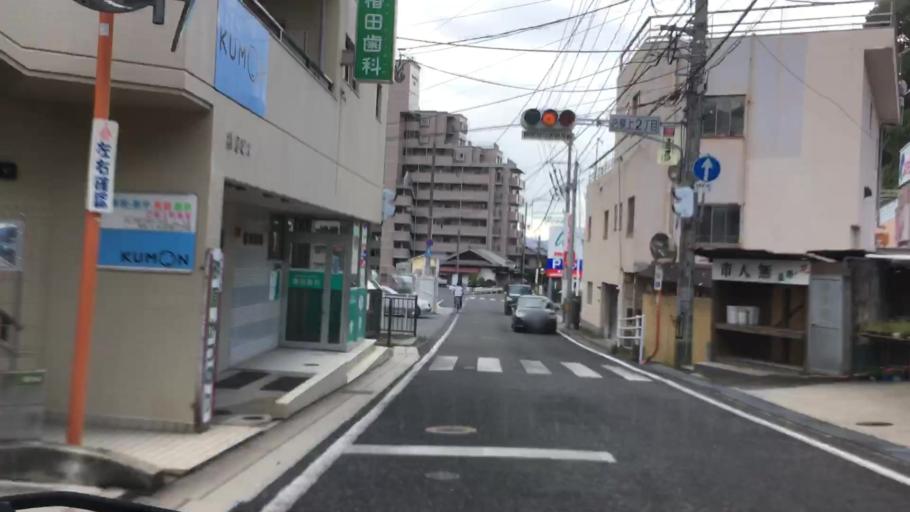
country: JP
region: Hiroshima
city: Hiroshima-shi
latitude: 34.4034
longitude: 132.4195
